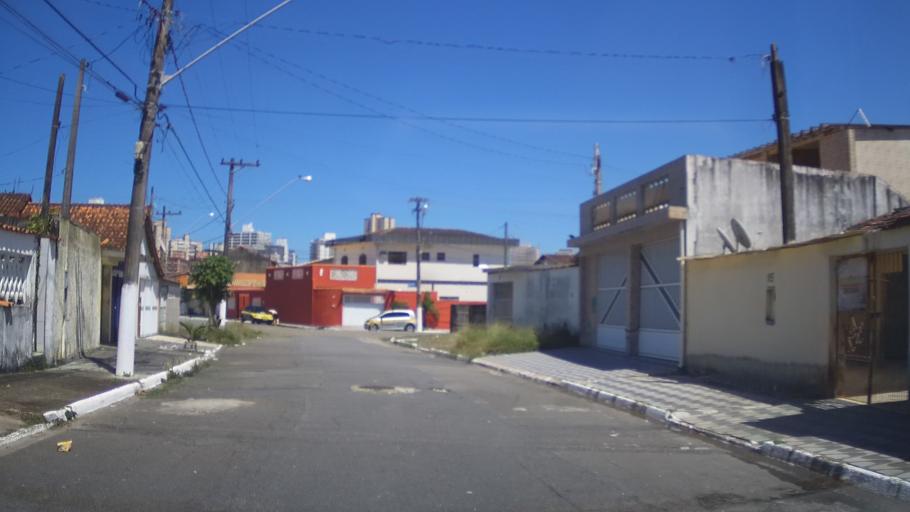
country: BR
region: Sao Paulo
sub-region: Mongagua
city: Mongagua
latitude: -24.0445
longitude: -46.5231
